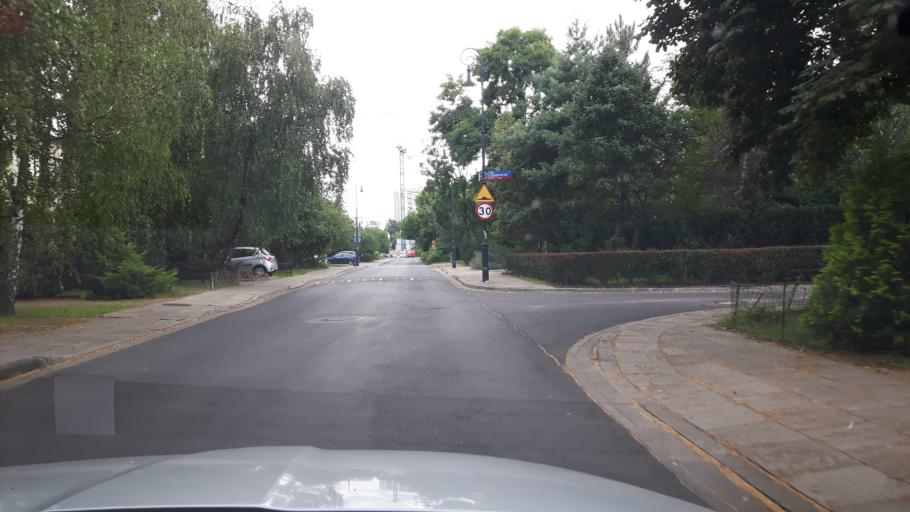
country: PL
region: Masovian Voivodeship
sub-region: Warszawa
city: Wilanow
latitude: 52.1789
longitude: 21.0635
